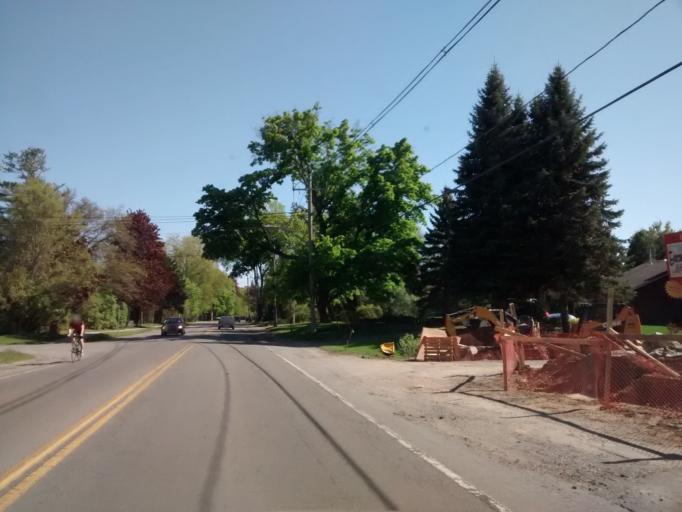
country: CA
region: Ontario
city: Oakville
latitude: 43.4229
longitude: -79.6895
